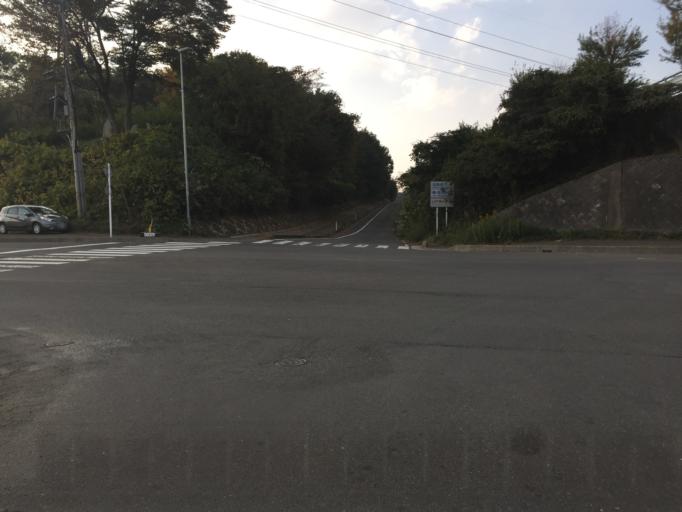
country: JP
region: Fukushima
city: Fukushima-shi
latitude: 37.6839
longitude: 140.4717
